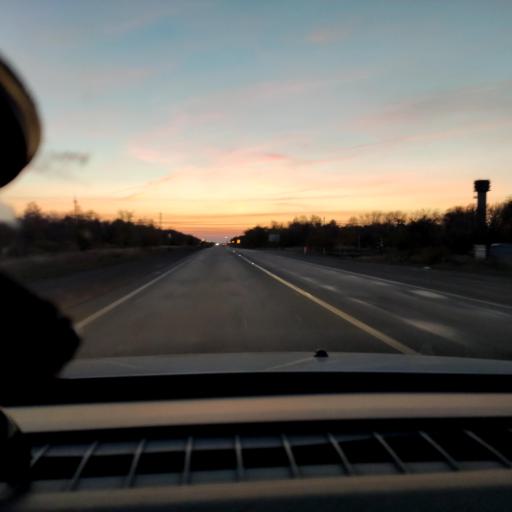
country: RU
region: Samara
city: Chapayevsk
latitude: 52.9969
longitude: 49.7805
